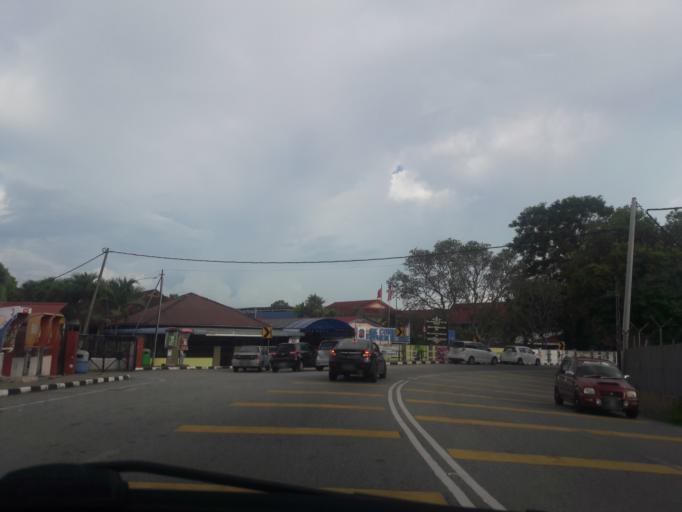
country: MY
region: Kedah
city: Sungai Petani
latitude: 5.6515
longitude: 100.4893
